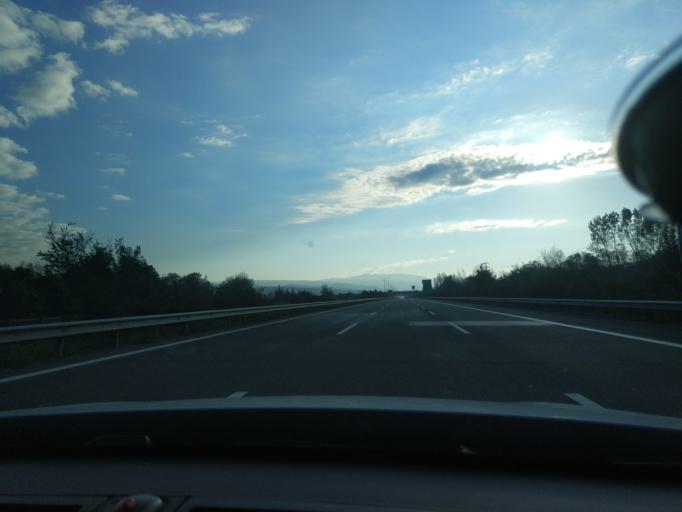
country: TR
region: Duzce
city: Duzce
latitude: 40.7908
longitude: 31.2271
